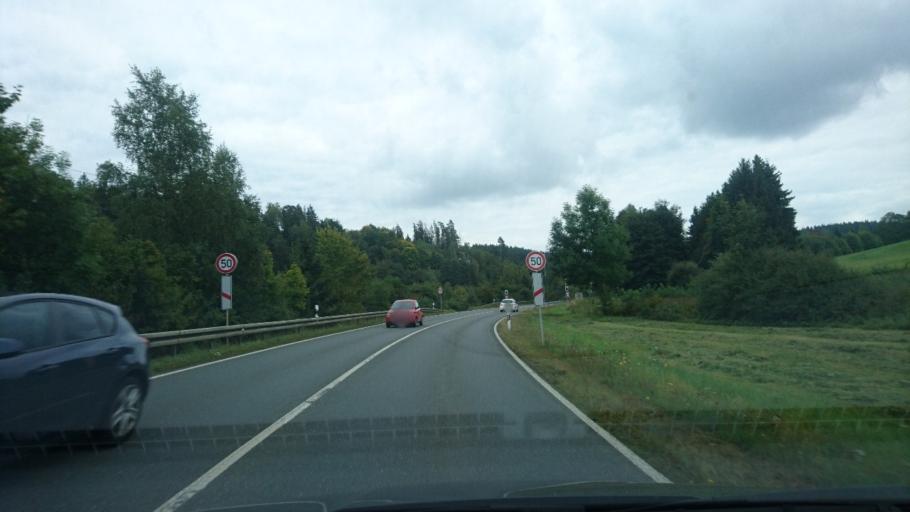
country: DE
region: Bavaria
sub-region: Upper Franconia
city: Naila
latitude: 50.3541
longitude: 11.7010
